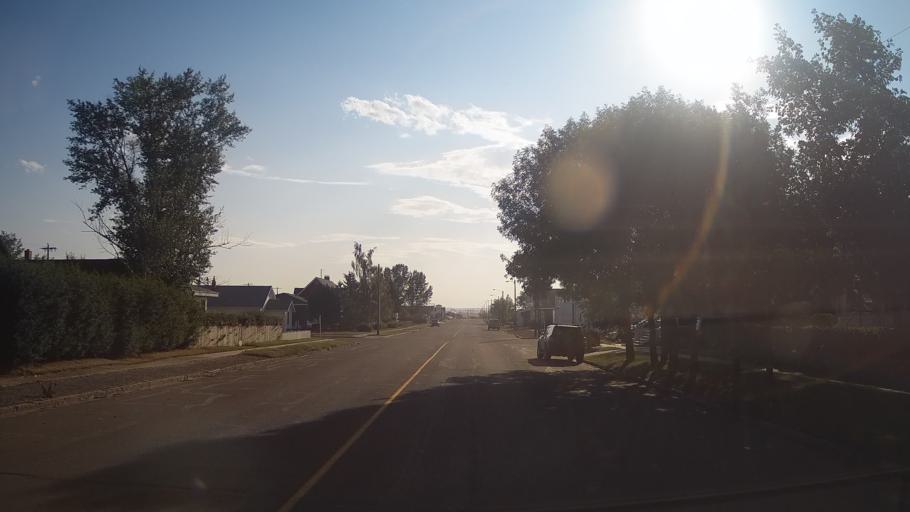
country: CA
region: Alberta
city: Hanna
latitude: 51.6417
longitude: -111.9344
